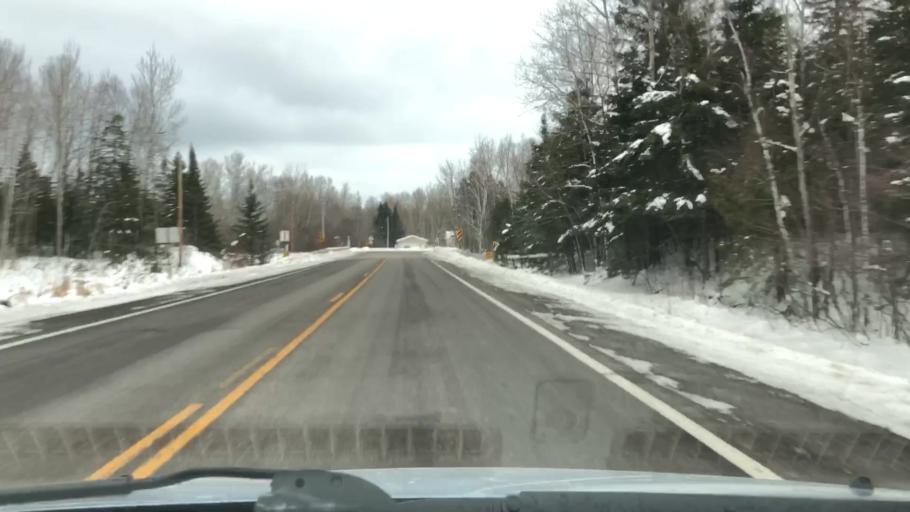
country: US
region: Minnesota
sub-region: Carlton County
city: Carlton
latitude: 46.6653
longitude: -92.3860
